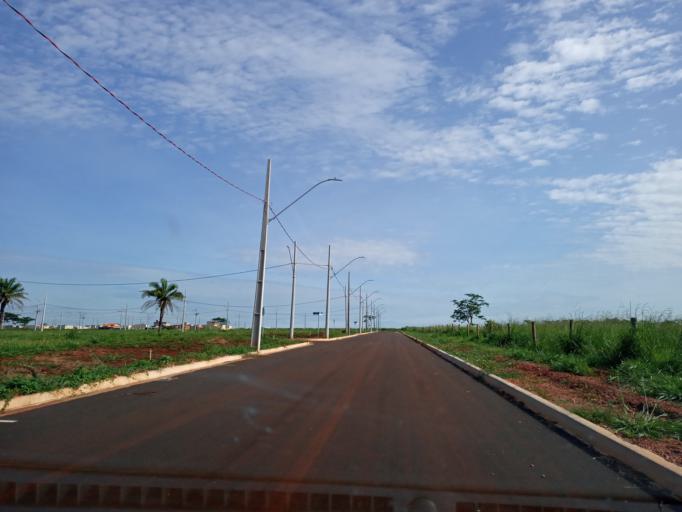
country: BR
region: Goias
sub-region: Itumbiara
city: Itumbiara
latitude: -18.4321
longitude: -49.1798
